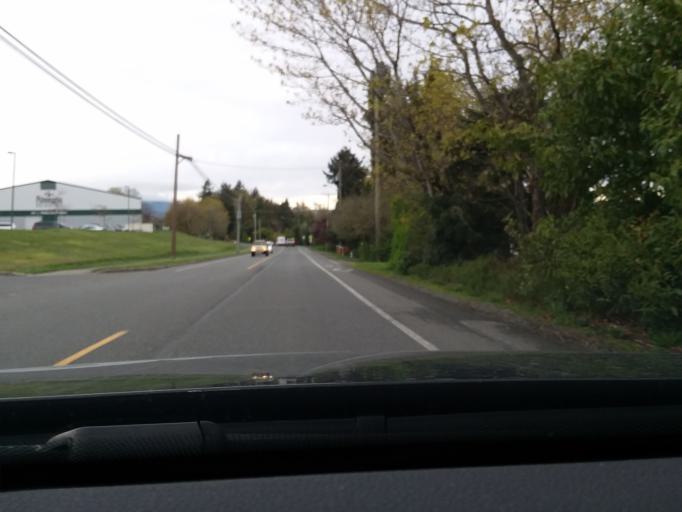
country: CA
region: British Columbia
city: North Saanich
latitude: 48.6229
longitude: -123.4182
